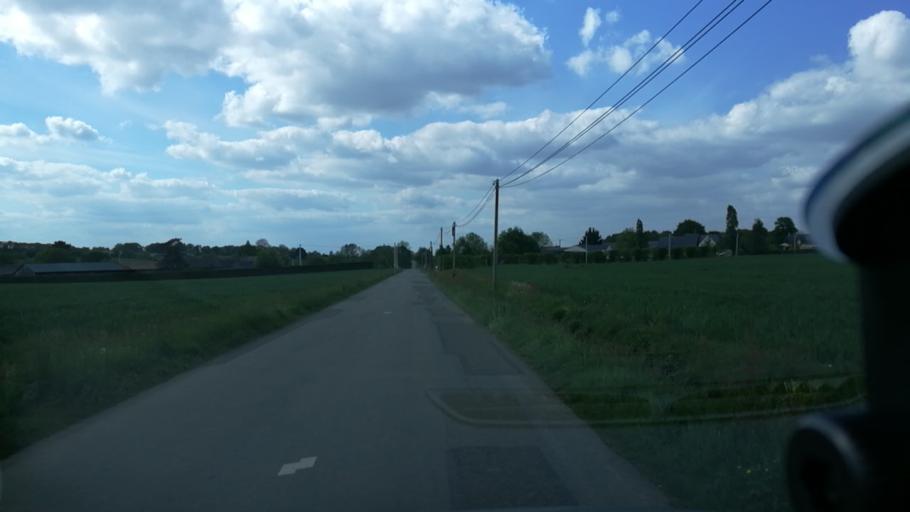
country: FR
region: Brittany
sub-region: Departement d'Ille-et-Vilaine
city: Martigne-Ferchaud
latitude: 47.8834
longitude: -1.3229
